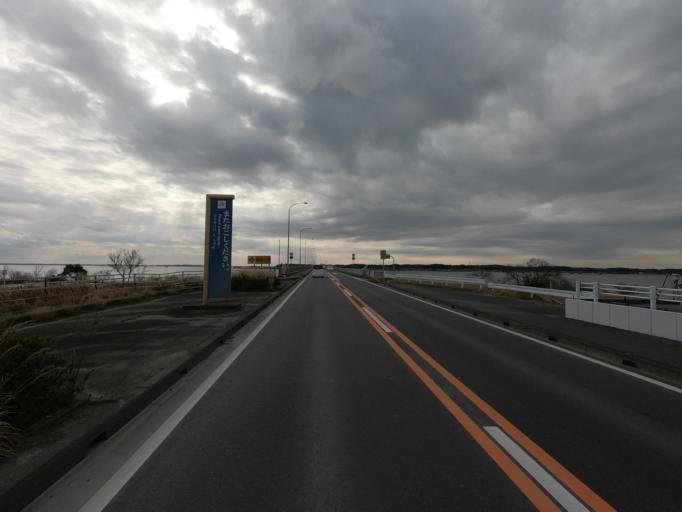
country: JP
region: Ibaraki
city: Inashiki
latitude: 36.0952
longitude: 140.4027
